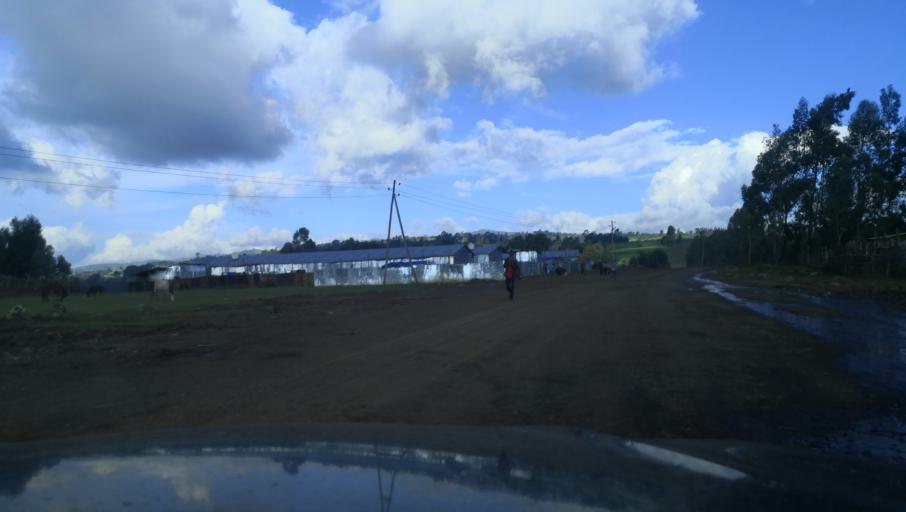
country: ET
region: Oromiya
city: Tulu Bolo
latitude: 8.4073
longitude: 38.2754
